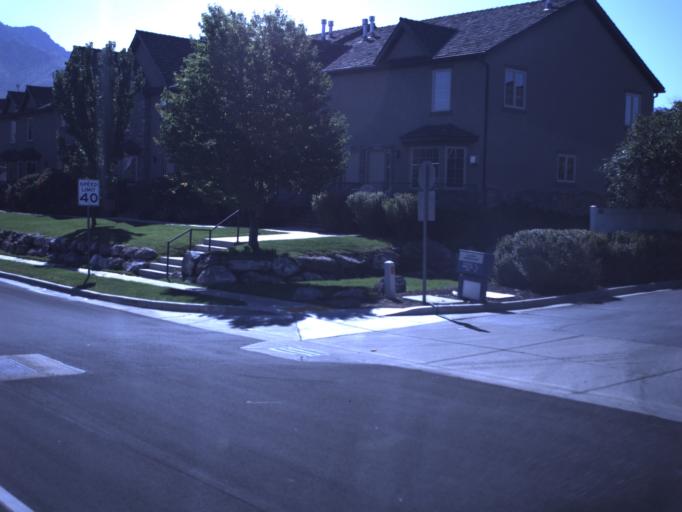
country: US
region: Utah
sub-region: Salt Lake County
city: Millcreek
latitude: 40.6743
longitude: -111.8533
